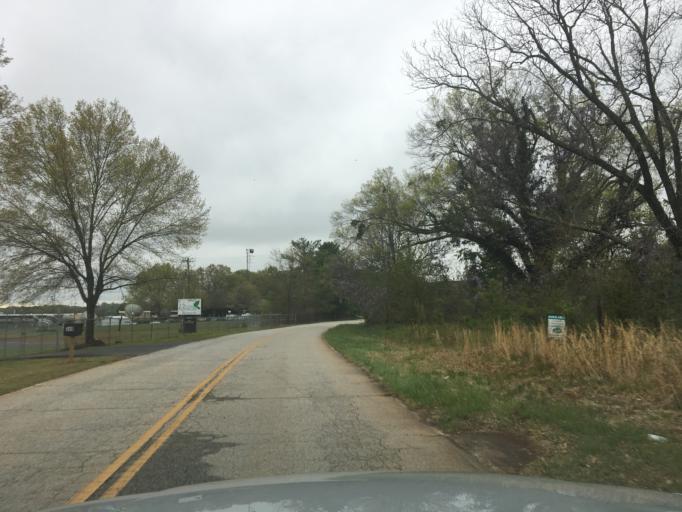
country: US
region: South Carolina
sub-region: Spartanburg County
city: Southern Shops
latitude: 34.9738
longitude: -82.0035
